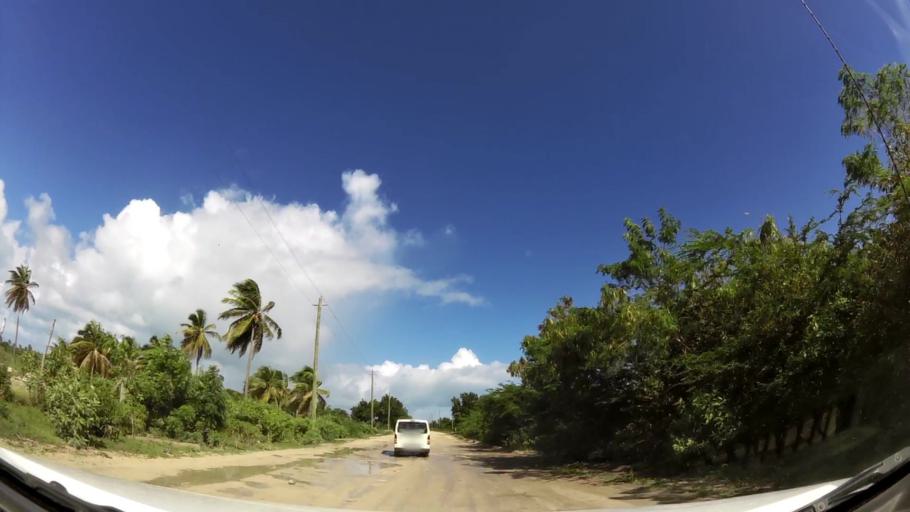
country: AG
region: Barbuda
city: Codrington
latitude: 17.6016
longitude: -61.8290
